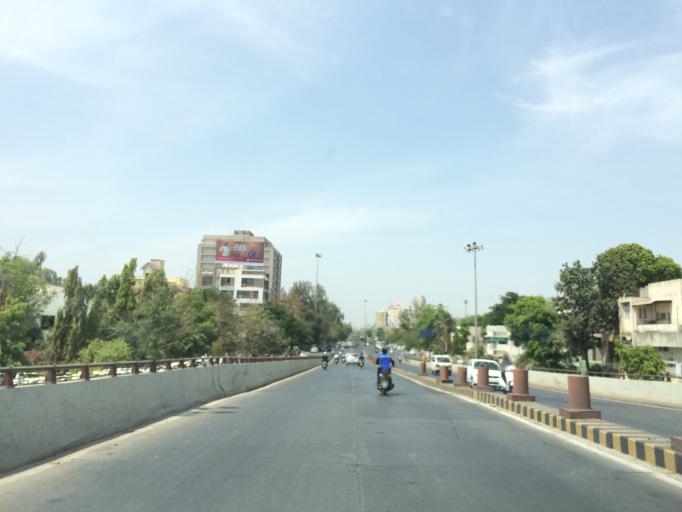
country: IN
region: Gujarat
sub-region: Ahmadabad
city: Ahmedabad
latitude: 23.0143
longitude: 72.5449
